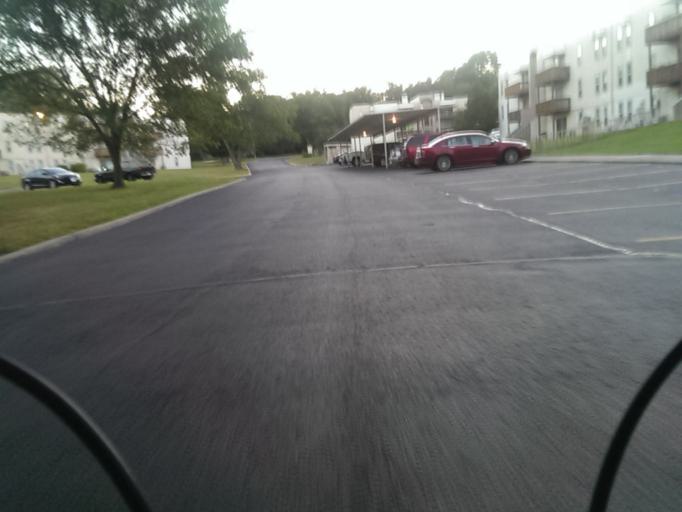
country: US
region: Missouri
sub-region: Jackson County
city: Grandview
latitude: 38.9159
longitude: -94.5777
